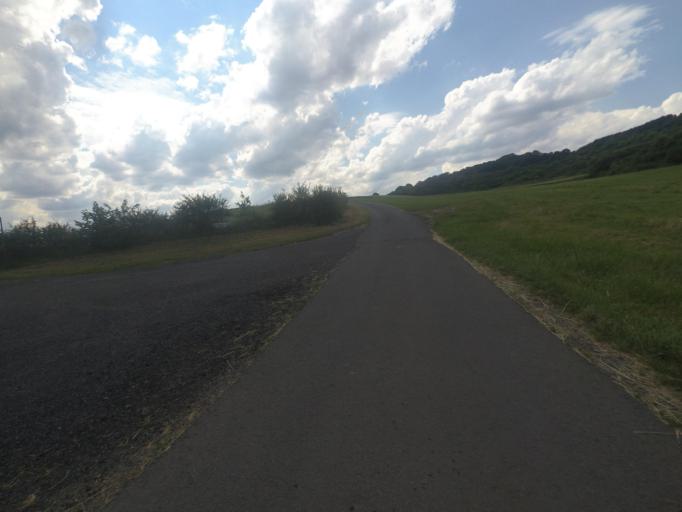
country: DE
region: Rheinland-Pfalz
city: Gerolstein
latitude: 50.2308
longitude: 6.6418
